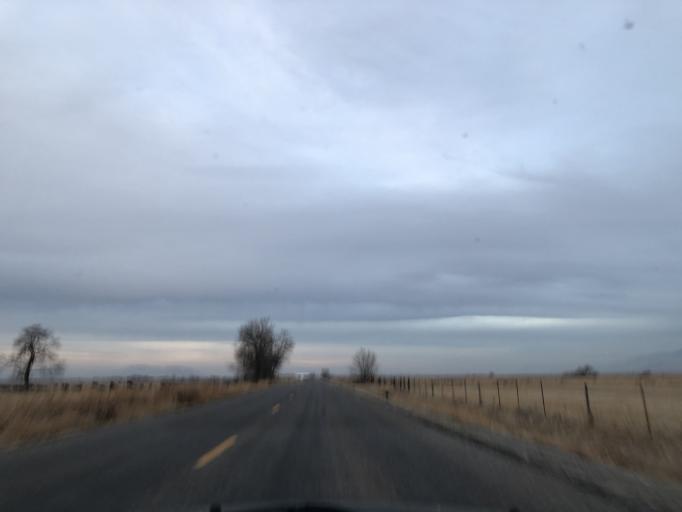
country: US
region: Utah
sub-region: Cache County
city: Benson
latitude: 41.7460
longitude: -111.9115
